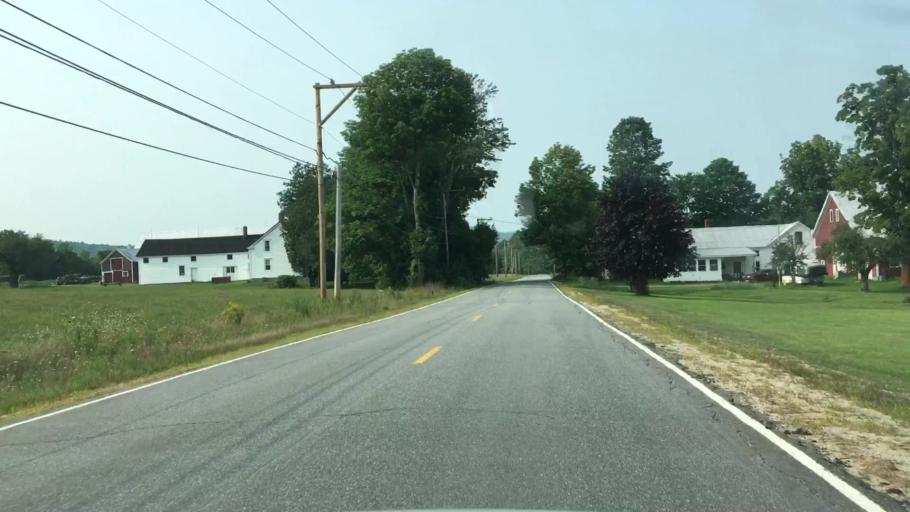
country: US
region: Maine
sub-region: Oxford County
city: Norway
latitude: 44.2260
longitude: -70.5940
